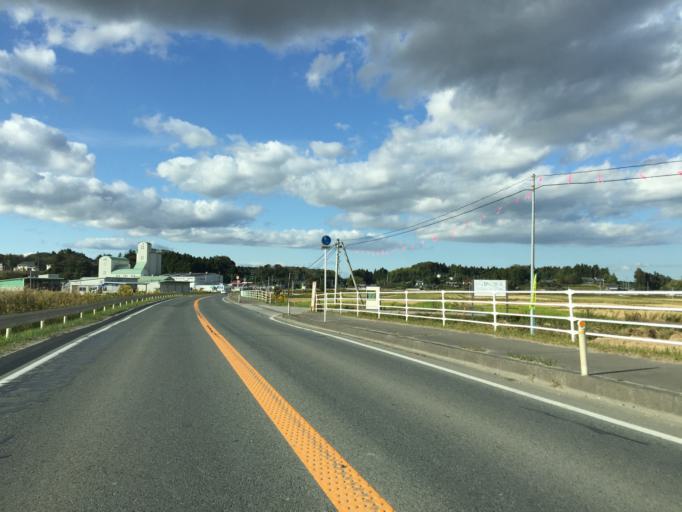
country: JP
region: Miyagi
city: Marumori
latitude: 37.8783
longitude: 140.9165
